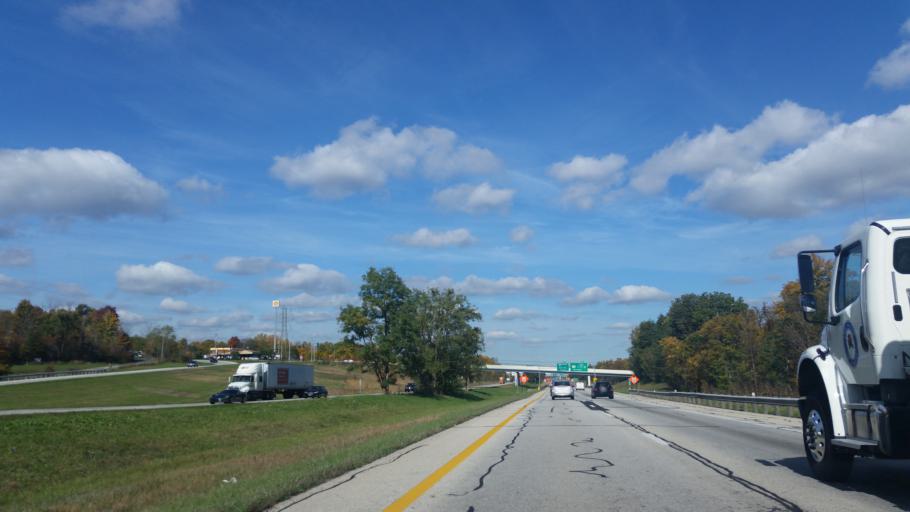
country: US
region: Ohio
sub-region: Summit County
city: Richfield
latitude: 41.2179
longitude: -81.6261
